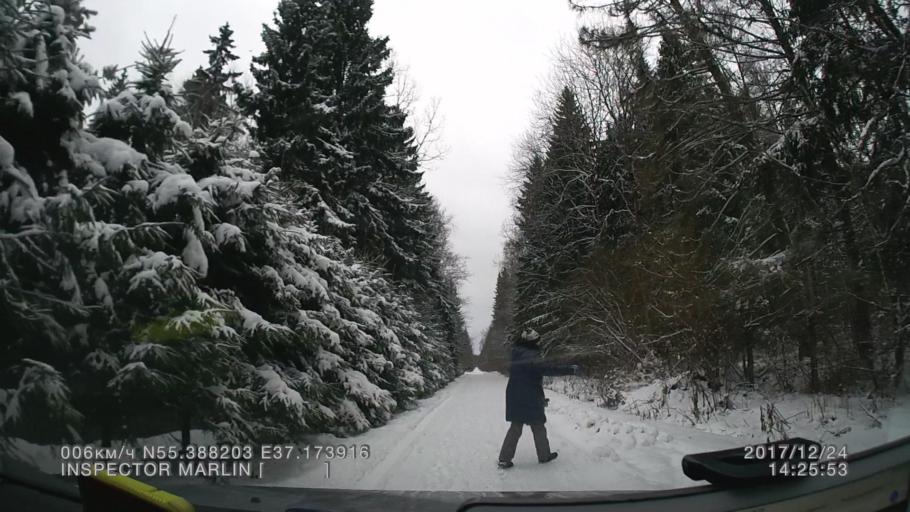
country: RU
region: Moskovskaya
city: Troitsk
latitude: 55.3881
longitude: 37.1738
